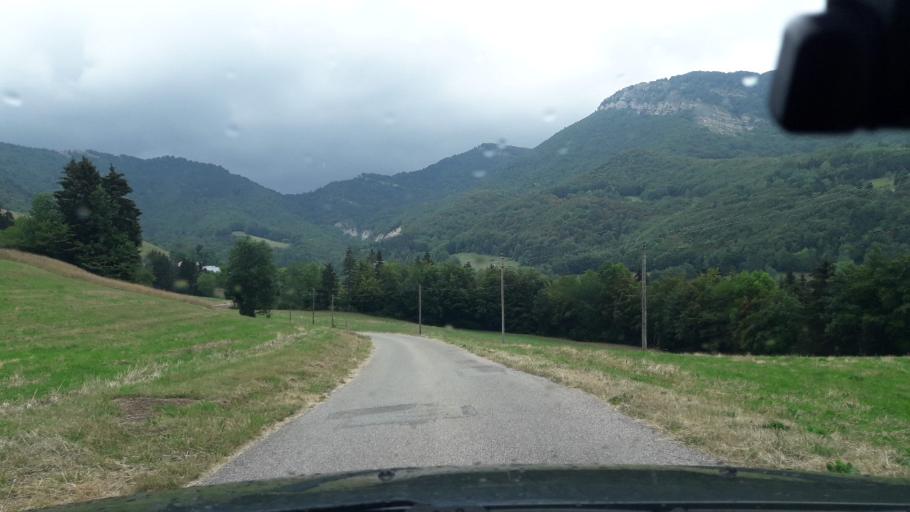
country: FR
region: Rhone-Alpes
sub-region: Departement de la Savoie
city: Vimines
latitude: 45.4749
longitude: 5.8857
